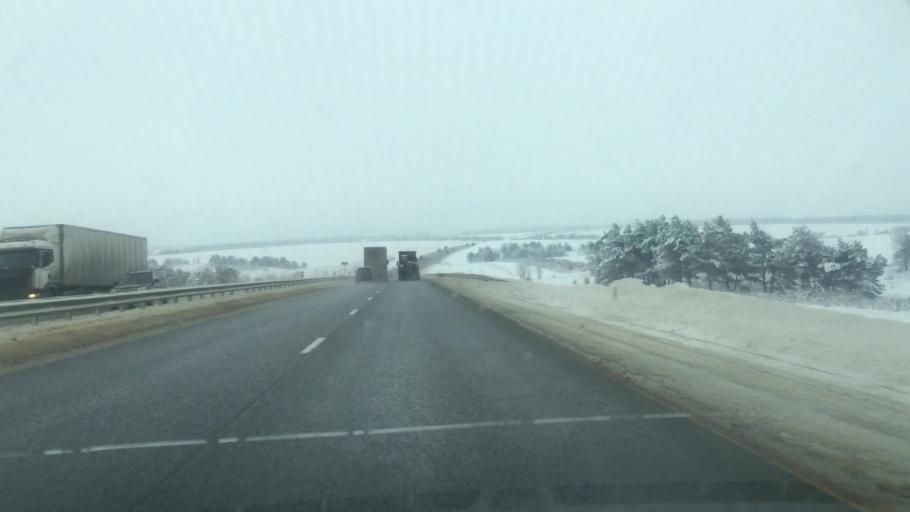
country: RU
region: Lipetsk
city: Stanovoye
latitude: 52.7915
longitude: 38.3507
